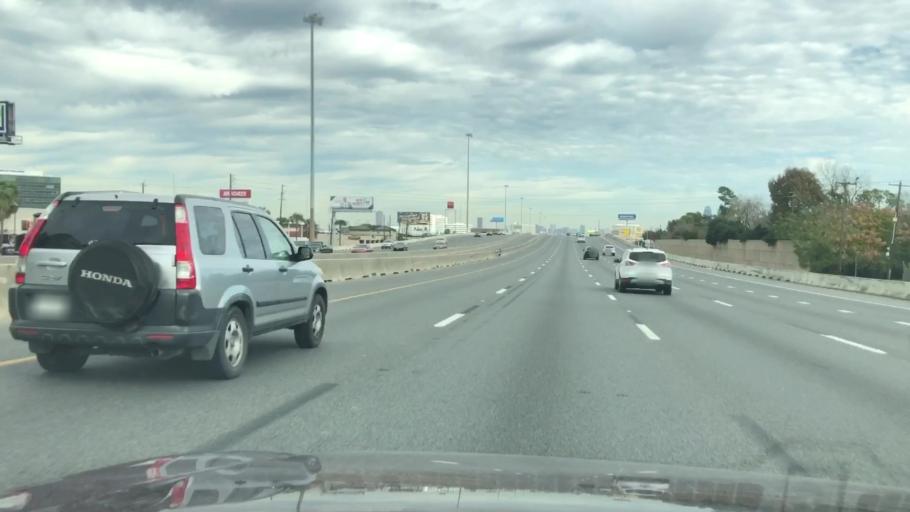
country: US
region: Texas
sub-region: Harris County
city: Bellaire
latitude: 29.7017
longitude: -95.5160
